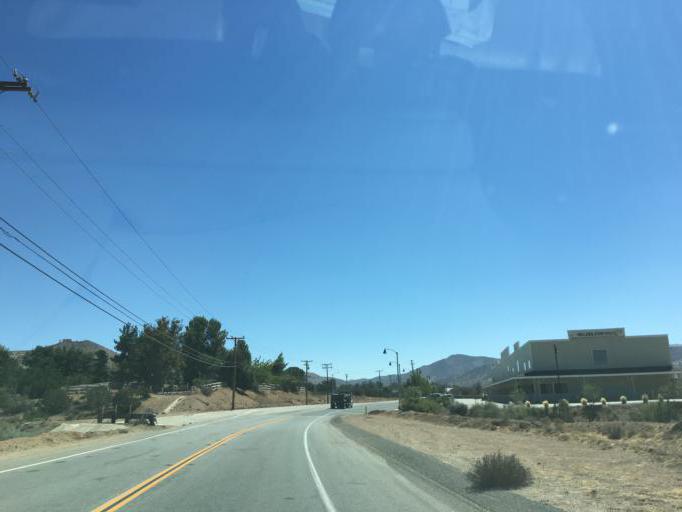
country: US
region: California
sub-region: Los Angeles County
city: Acton
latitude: 34.4807
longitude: -118.1650
